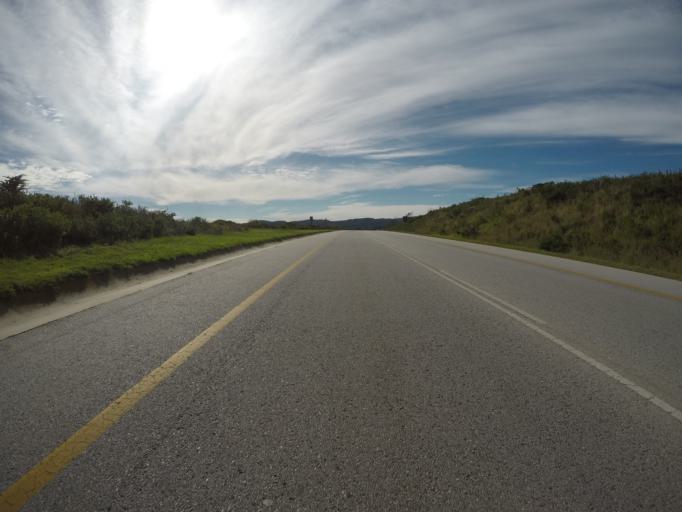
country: ZA
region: Eastern Cape
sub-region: Cacadu District Municipality
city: Jeffrey's Bay
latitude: -33.8967
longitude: 25.1220
